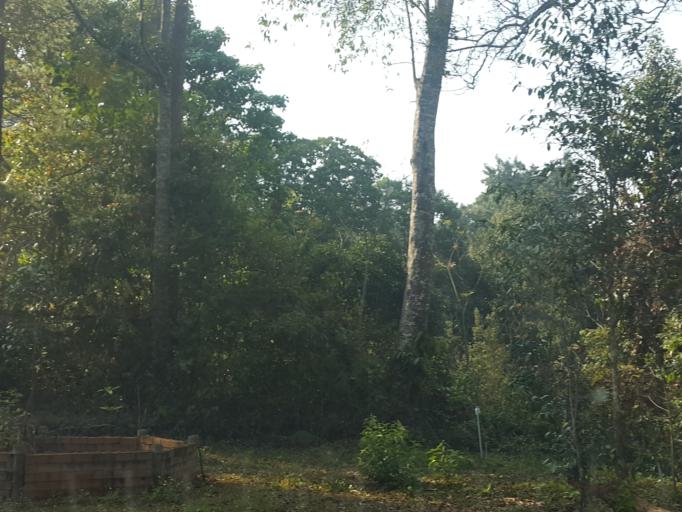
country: TH
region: Chiang Mai
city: Samoeng
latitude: 19.0160
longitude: 98.7575
